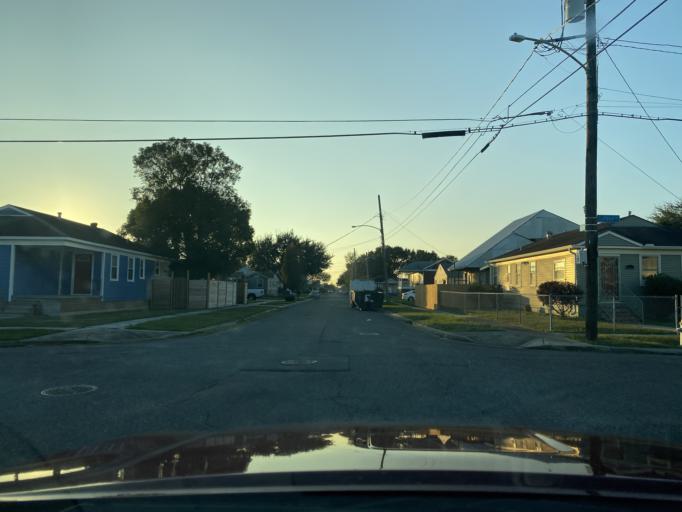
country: US
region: Louisiana
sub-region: Orleans Parish
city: New Orleans
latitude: 30.0206
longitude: -90.0493
